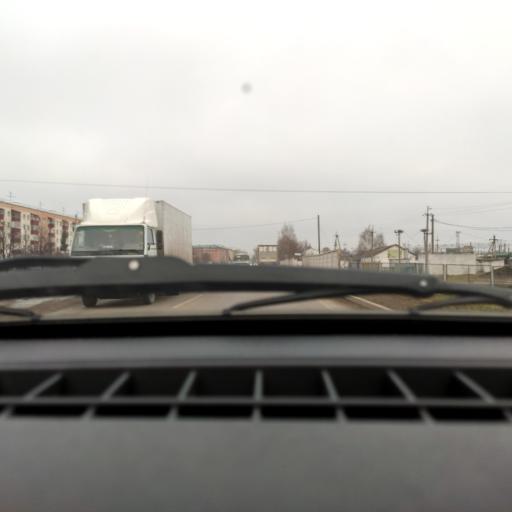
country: RU
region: Bashkortostan
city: Chishmy
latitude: 54.5870
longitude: 55.3911
